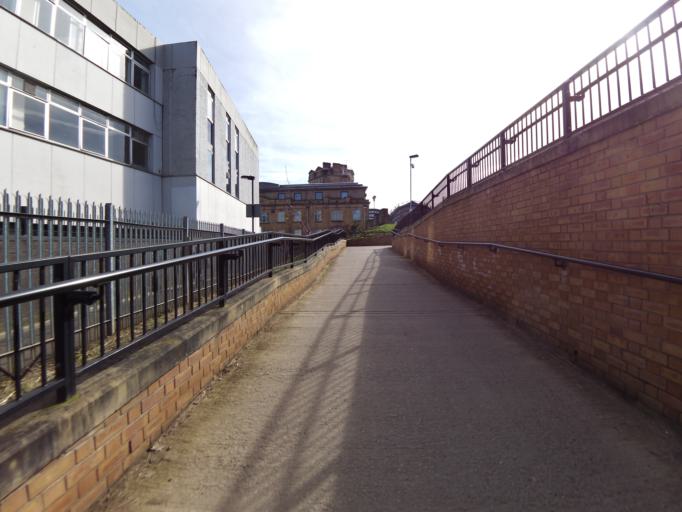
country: GB
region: England
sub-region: City of York
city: York
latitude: 53.9604
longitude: -1.0929
